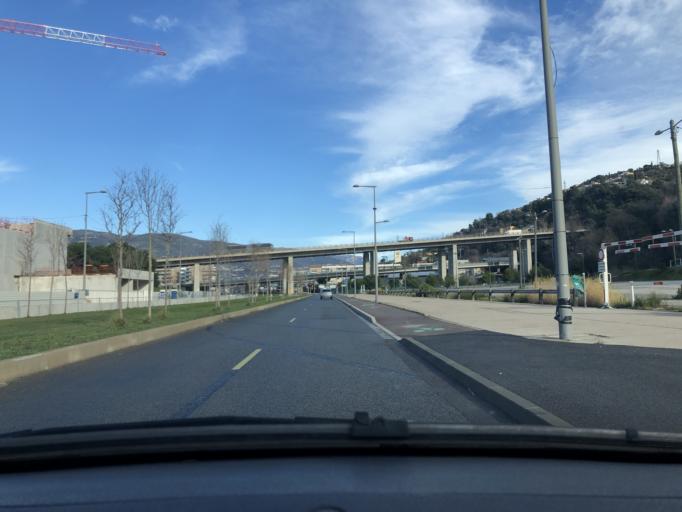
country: FR
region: Provence-Alpes-Cote d'Azur
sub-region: Departement des Alpes-Maritimes
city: Saint-Laurent-du-Var
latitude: 43.7069
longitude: 7.1963
